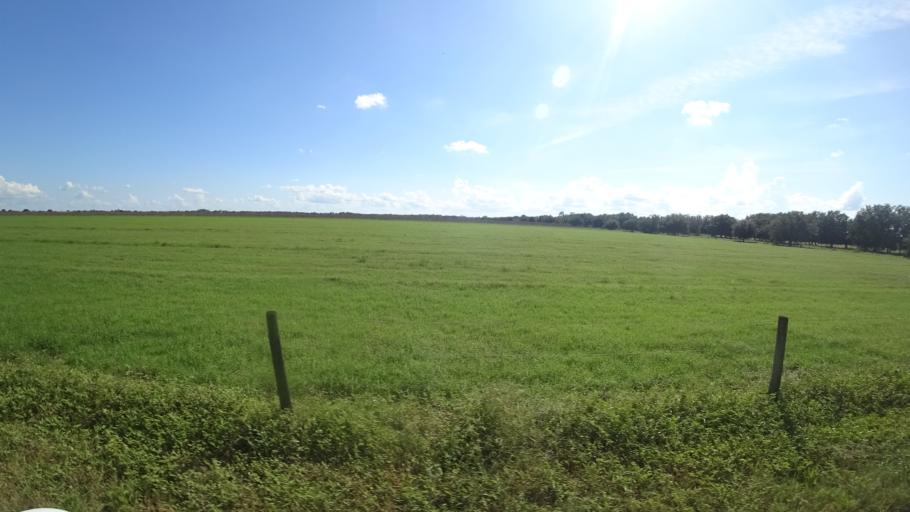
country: US
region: Florida
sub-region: Sarasota County
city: The Meadows
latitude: 27.4308
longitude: -82.2942
